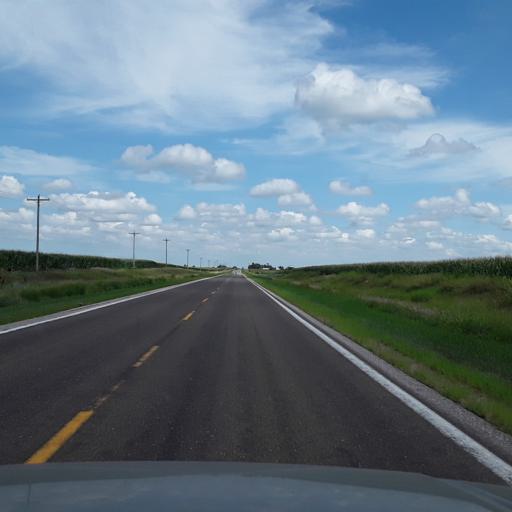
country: US
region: Nebraska
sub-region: Polk County
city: Osceola
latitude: 41.0519
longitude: -97.4064
